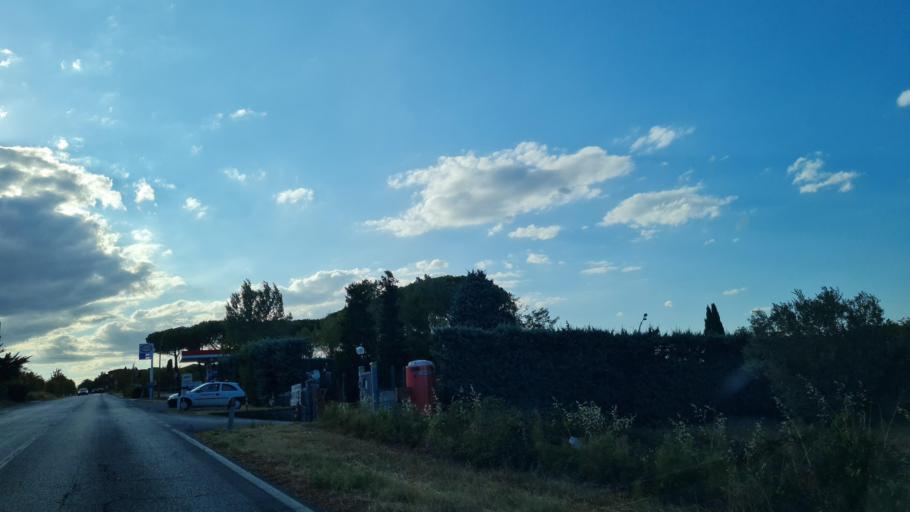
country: IT
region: Tuscany
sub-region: Provincia di Siena
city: Chianciano Terme
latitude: 43.0348
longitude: 11.8417
